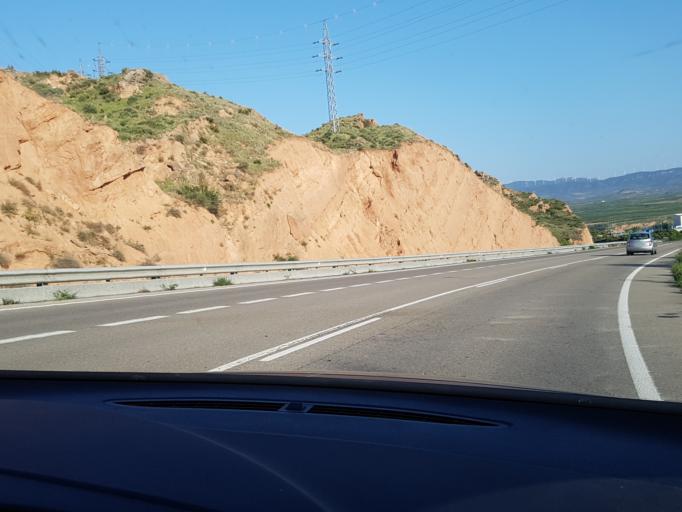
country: ES
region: La Rioja
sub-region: Provincia de La Rioja
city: Arnedo
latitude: 42.2387
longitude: -2.0864
